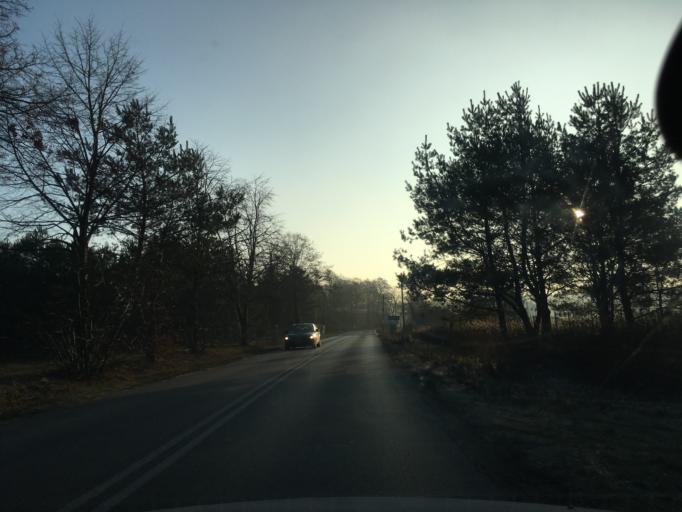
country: PL
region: Masovian Voivodeship
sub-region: Powiat piaseczynski
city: Lesznowola
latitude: 52.0739
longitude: 20.9726
